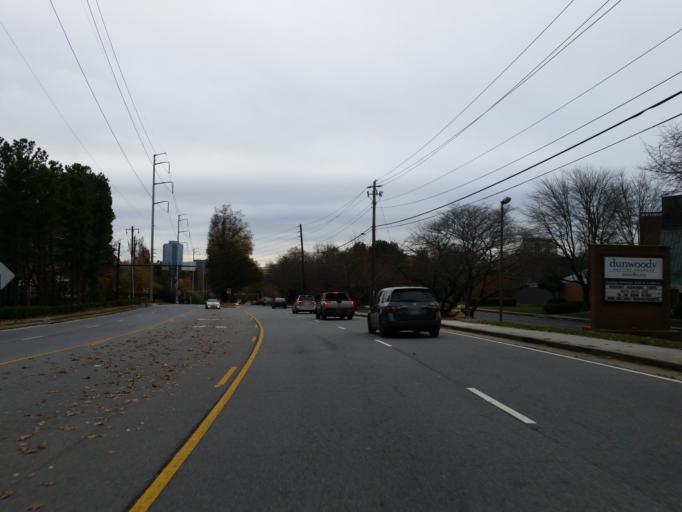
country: US
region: Georgia
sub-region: DeKalb County
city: Dunwoody
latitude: 33.9417
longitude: -84.3383
